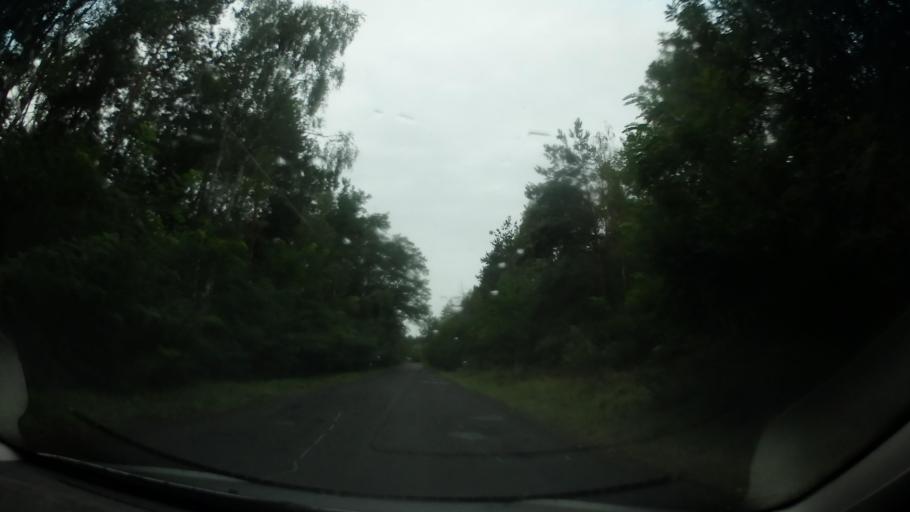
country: CZ
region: Central Bohemia
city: Milovice
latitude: 50.2433
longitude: 14.9081
